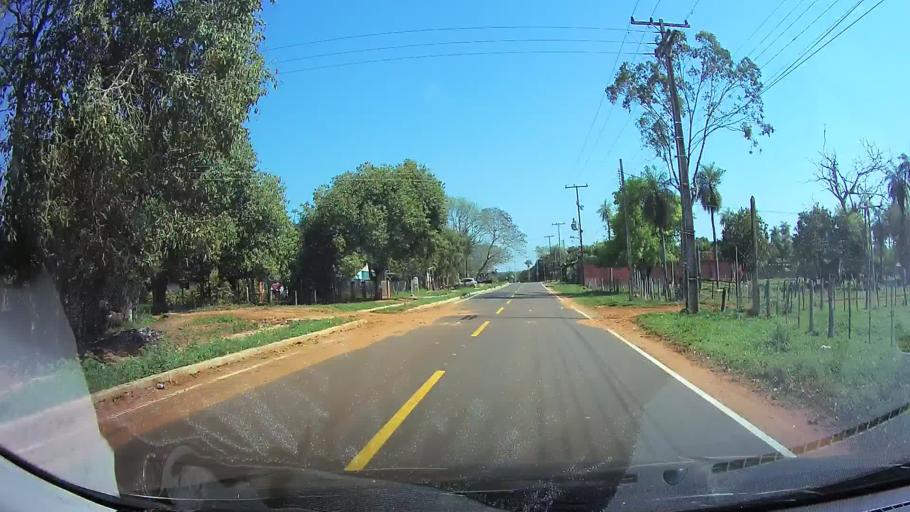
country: PY
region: Central
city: Limpio
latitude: -25.2249
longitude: -57.4879
